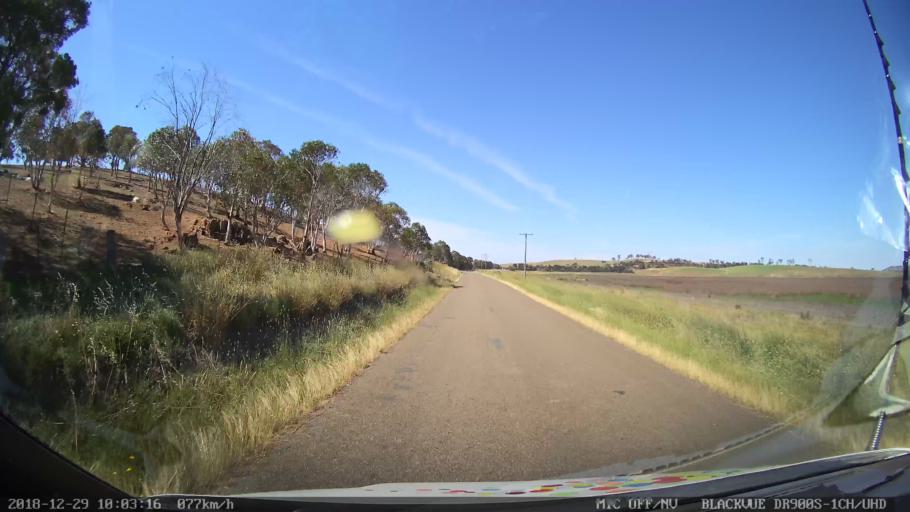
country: AU
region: New South Wales
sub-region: Goulburn Mulwaree
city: Goulburn
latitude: -34.8092
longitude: 149.4606
